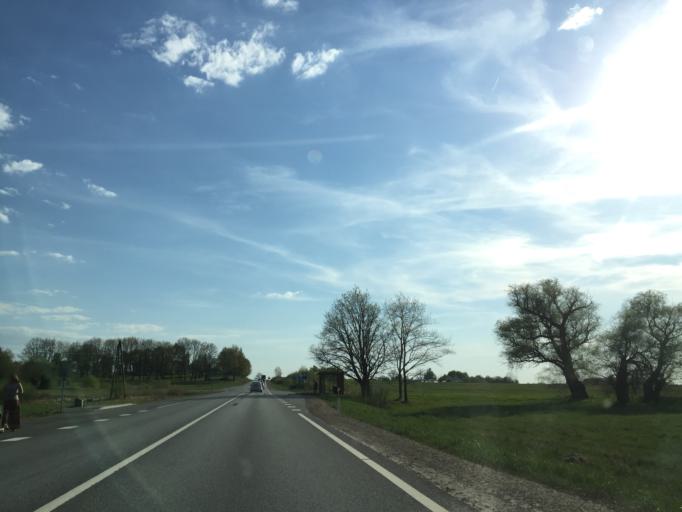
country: LV
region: Sigulda
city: Sigulda
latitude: 57.2634
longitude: 24.8762
